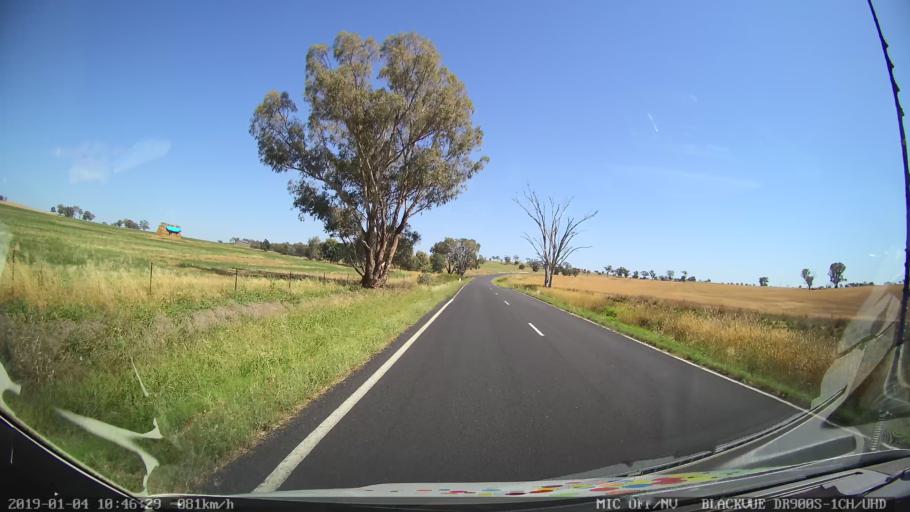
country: AU
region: New South Wales
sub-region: Cabonne
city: Molong
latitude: -33.2808
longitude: 148.7225
